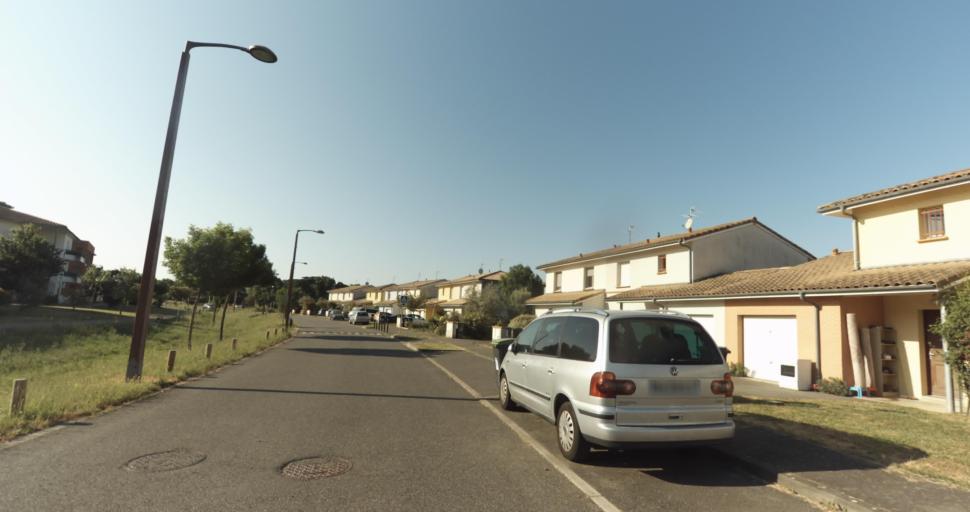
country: FR
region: Midi-Pyrenees
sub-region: Departement de la Haute-Garonne
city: La Salvetat-Saint-Gilles
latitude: 43.5715
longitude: 1.2438
